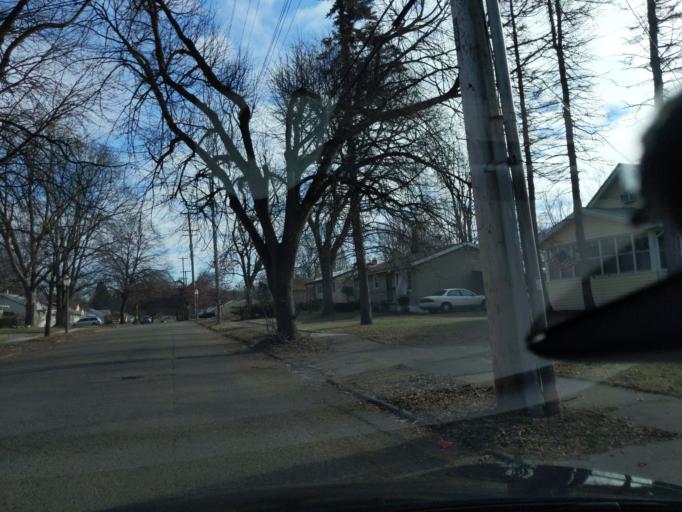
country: US
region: Michigan
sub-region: Ingham County
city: Lansing
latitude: 42.6930
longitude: -84.5812
